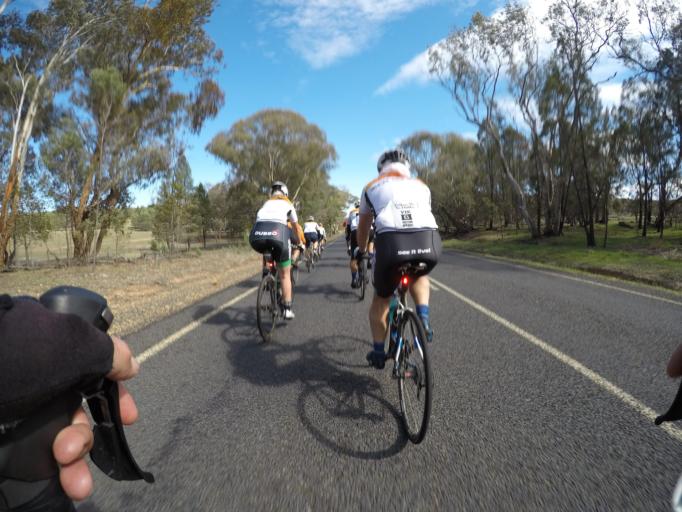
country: AU
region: New South Wales
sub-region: Parkes
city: Peak Hill
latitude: -32.7303
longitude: 148.5676
